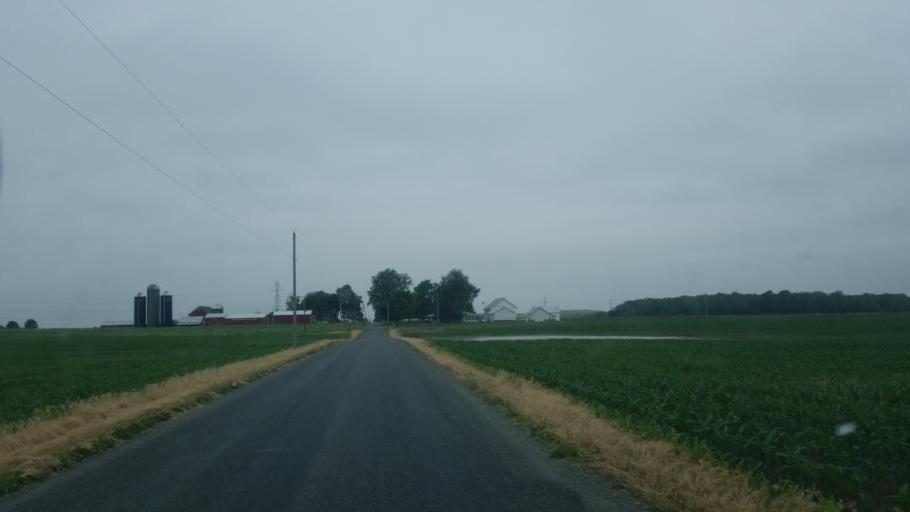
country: US
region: Indiana
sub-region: Marshall County
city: Bremen
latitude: 41.4938
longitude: -86.1345
